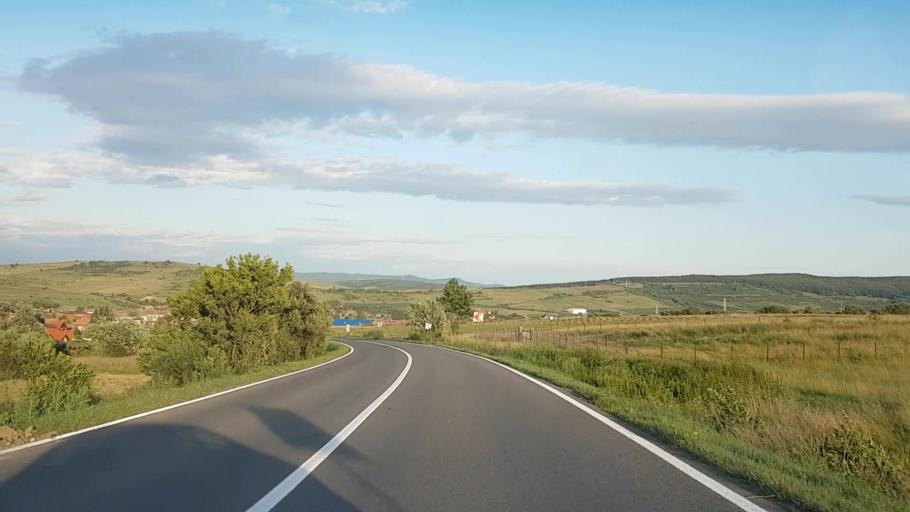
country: RO
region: Harghita
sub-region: Comuna Lupeni
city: Lupeni
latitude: 46.3720
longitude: 25.2221
